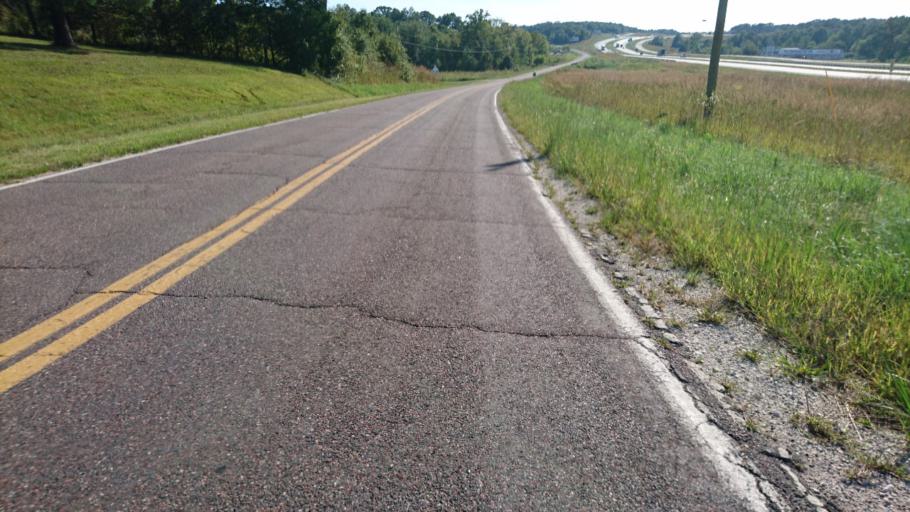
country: US
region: Missouri
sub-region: Crawford County
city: Bourbon
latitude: 38.1278
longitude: -91.3044
